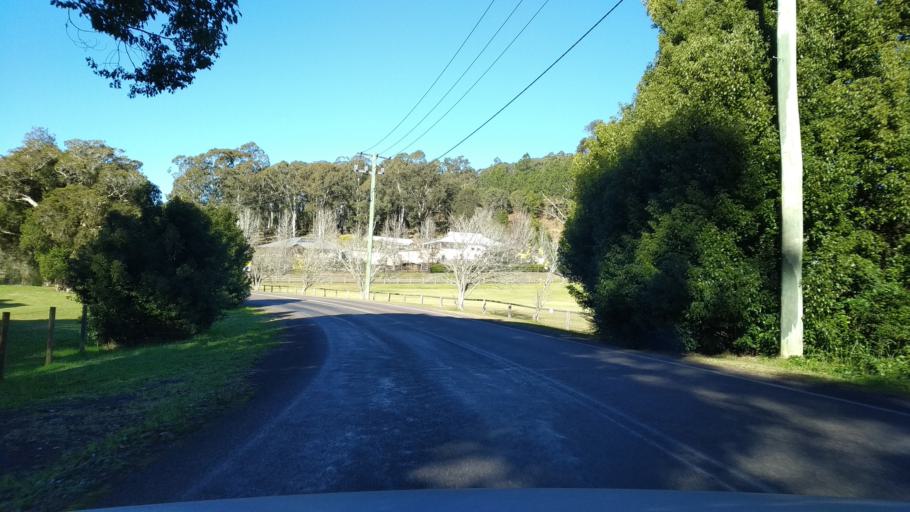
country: AU
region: New South Wales
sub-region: Wyong Shire
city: Little Jilliby
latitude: -33.2274
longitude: 151.2829
